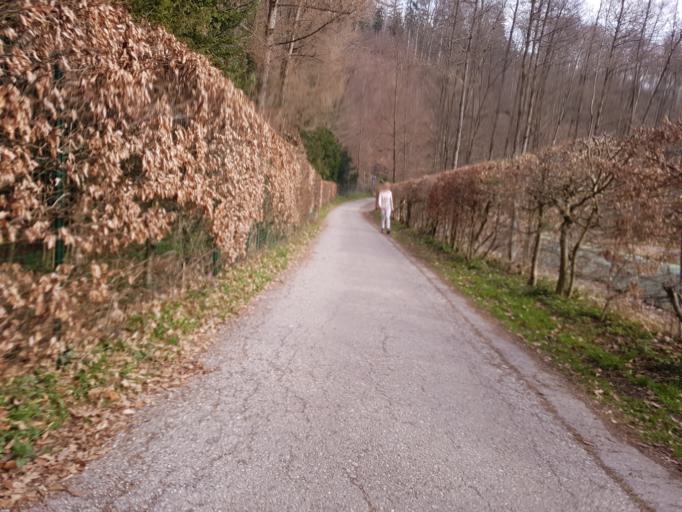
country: AT
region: Salzburg
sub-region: Politischer Bezirk Salzburg-Umgebung
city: Elsbethen
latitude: 47.7915
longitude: 13.0879
